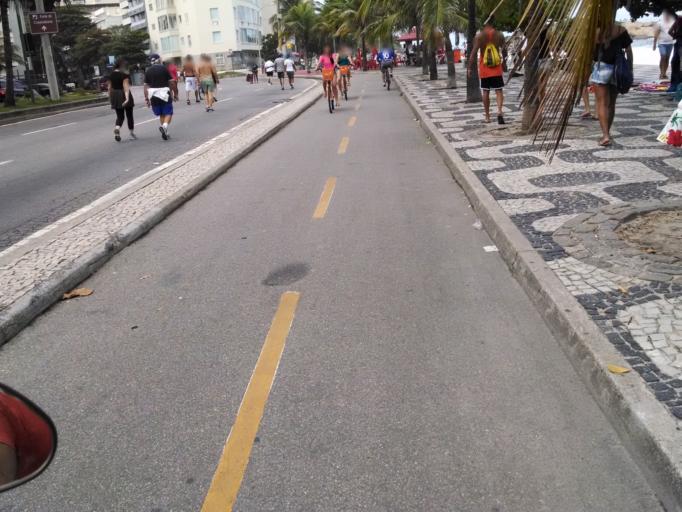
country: BR
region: Rio de Janeiro
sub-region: Rio De Janeiro
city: Rio de Janeiro
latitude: -22.9878
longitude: -43.1953
